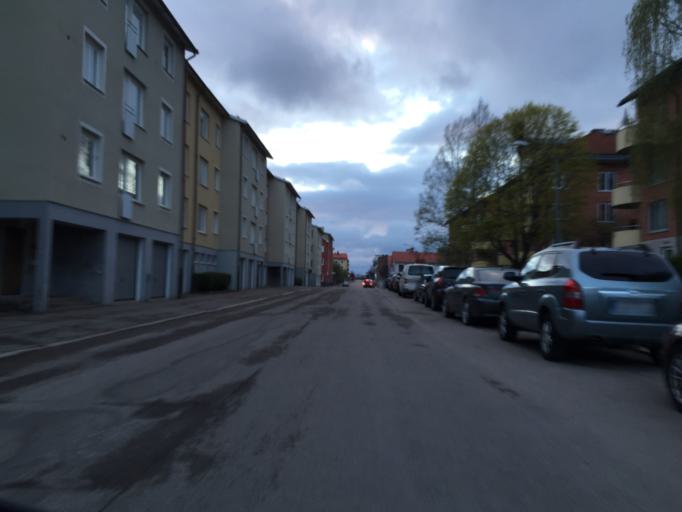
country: SE
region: Dalarna
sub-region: Ludvika Kommun
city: Ludvika
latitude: 60.1474
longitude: 15.1911
